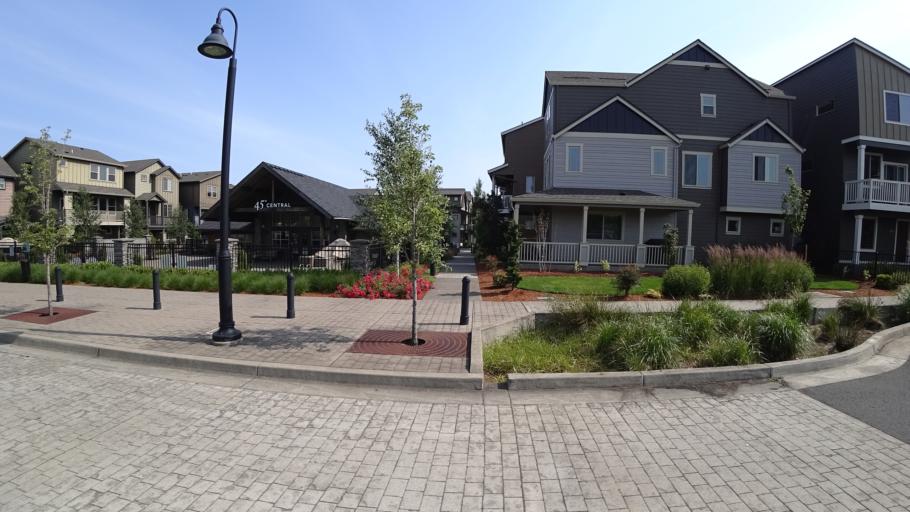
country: US
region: Oregon
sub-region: Washington County
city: Cedar Mill
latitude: 45.5044
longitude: -122.8238
